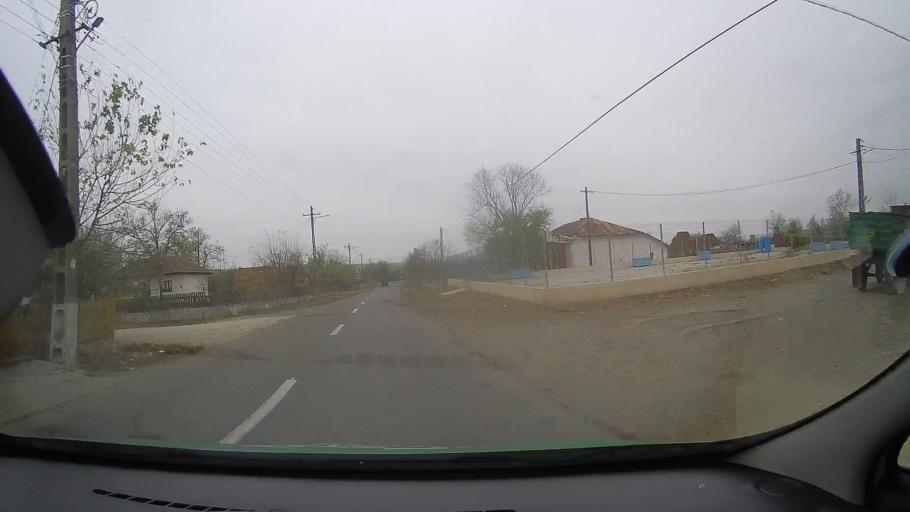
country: RO
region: Constanta
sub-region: Comuna Vulturu
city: Vulturu
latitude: 44.7022
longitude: 28.2371
